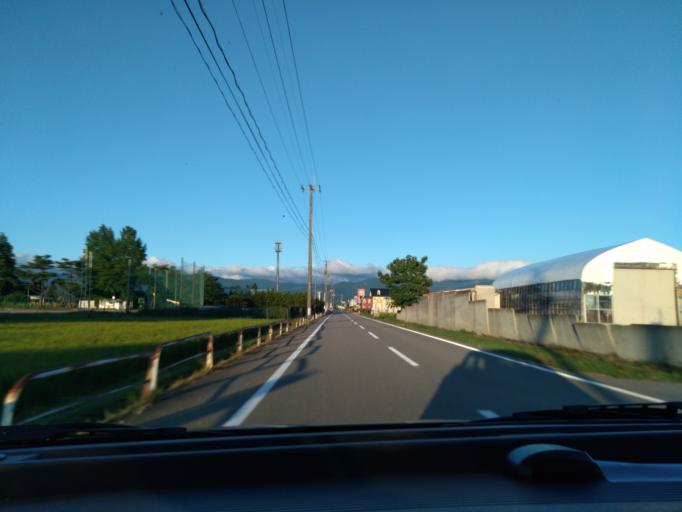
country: JP
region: Akita
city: Omagari
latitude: 39.4863
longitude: 140.5375
